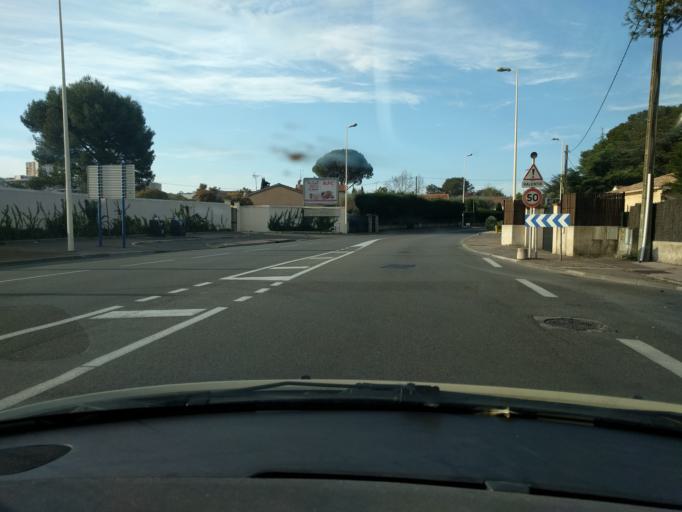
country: FR
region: Provence-Alpes-Cote d'Azur
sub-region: Departement des Alpes-Maritimes
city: Mougins
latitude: 43.5734
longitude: 6.9841
